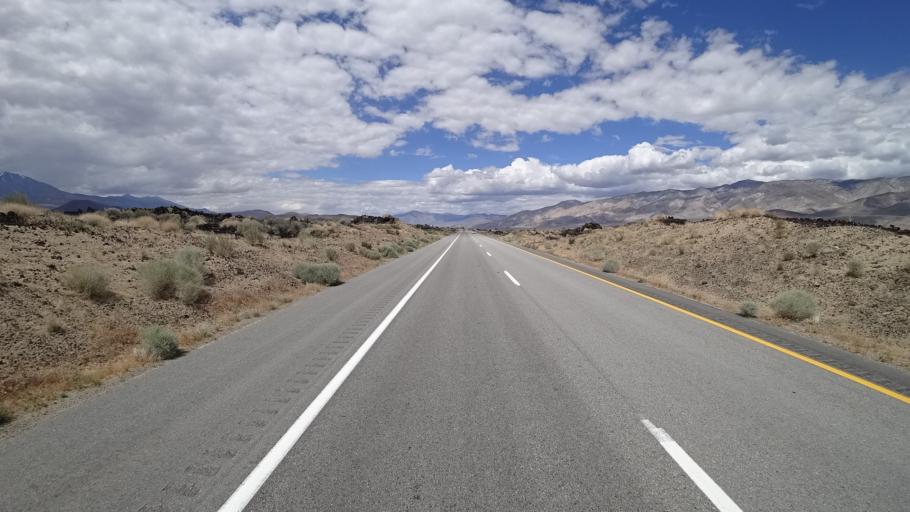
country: US
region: California
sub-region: Inyo County
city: Big Pine
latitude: 36.9835
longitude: -118.2359
